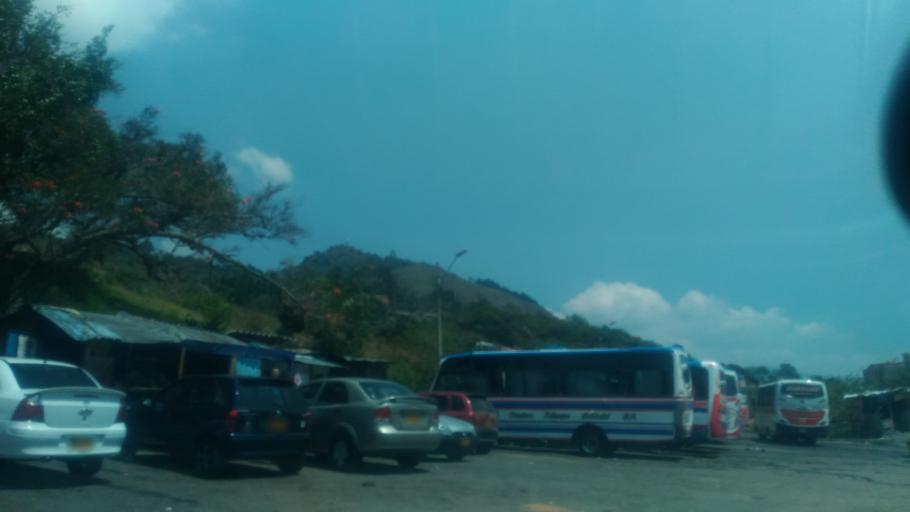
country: CO
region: Antioquia
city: Medellin
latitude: 6.2937
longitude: -75.5885
